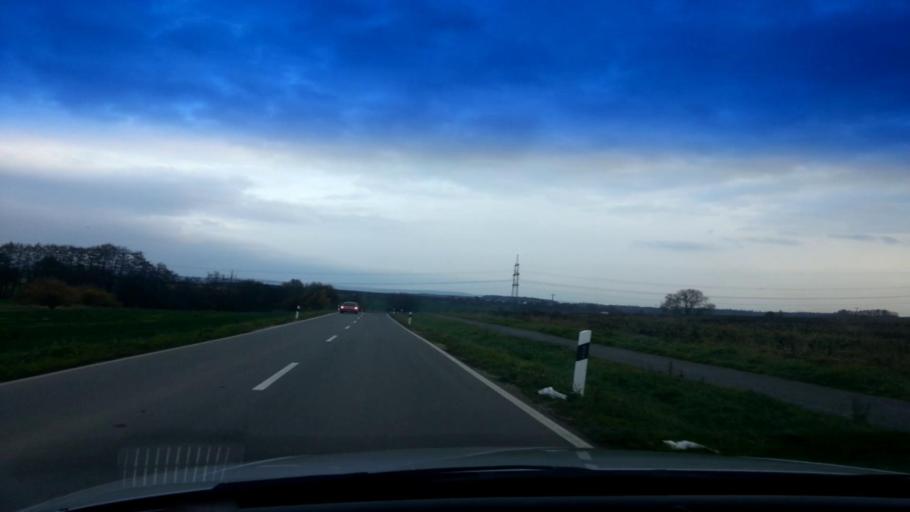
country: DE
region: Bavaria
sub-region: Upper Franconia
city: Memmelsdorf
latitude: 49.9574
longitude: 10.9620
